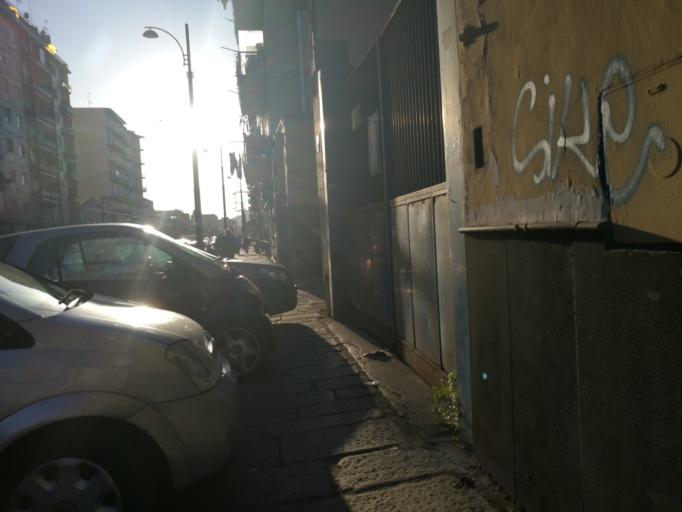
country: IT
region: Campania
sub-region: Provincia di Napoli
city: Napoli
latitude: 40.8627
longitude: 14.2828
